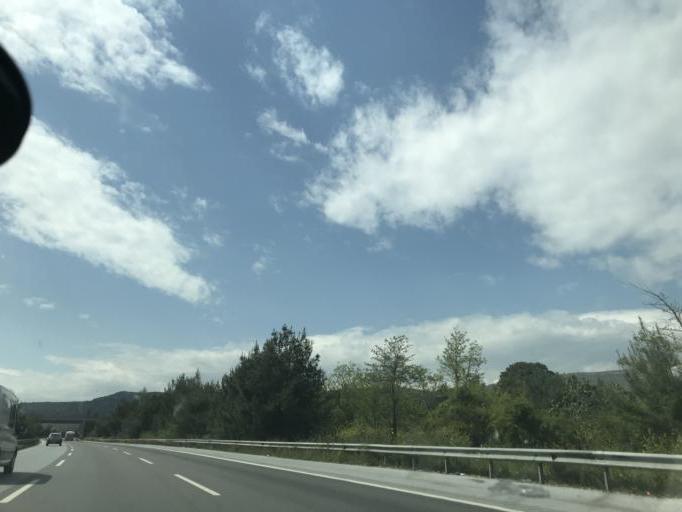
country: TR
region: Mersin
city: Tarsus
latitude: 37.1313
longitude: 34.8758
